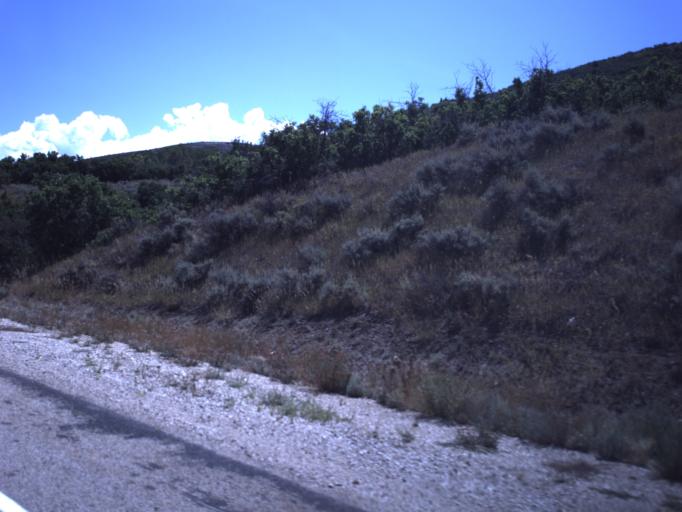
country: US
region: Utah
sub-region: Summit County
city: Francis
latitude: 40.5951
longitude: -111.3638
